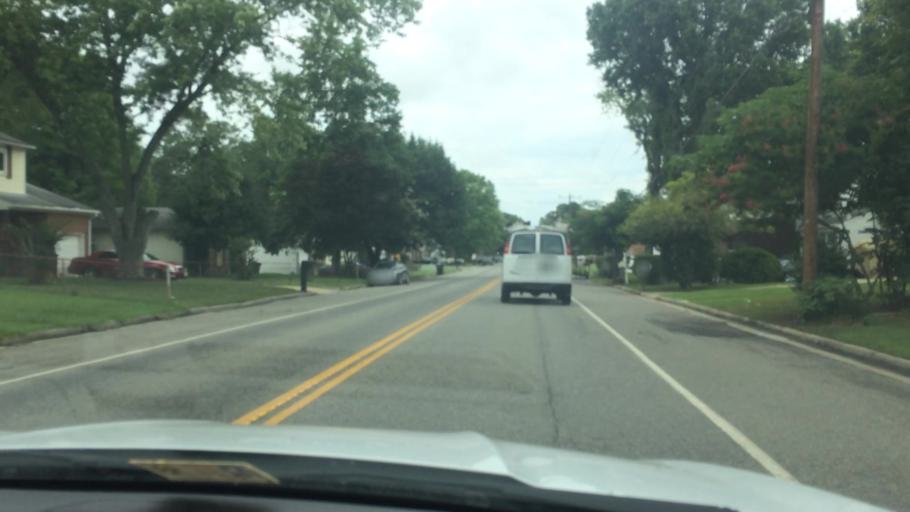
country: US
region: Virginia
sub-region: City of Williamsburg
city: Williamsburg
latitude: 37.2730
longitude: -76.6722
